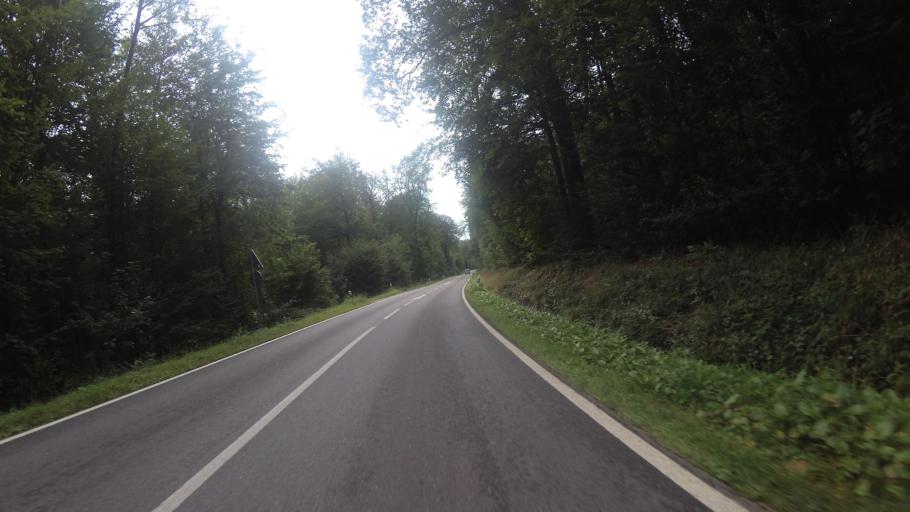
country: DE
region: Saarland
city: Saarbrucken
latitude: 49.2792
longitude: 6.9874
